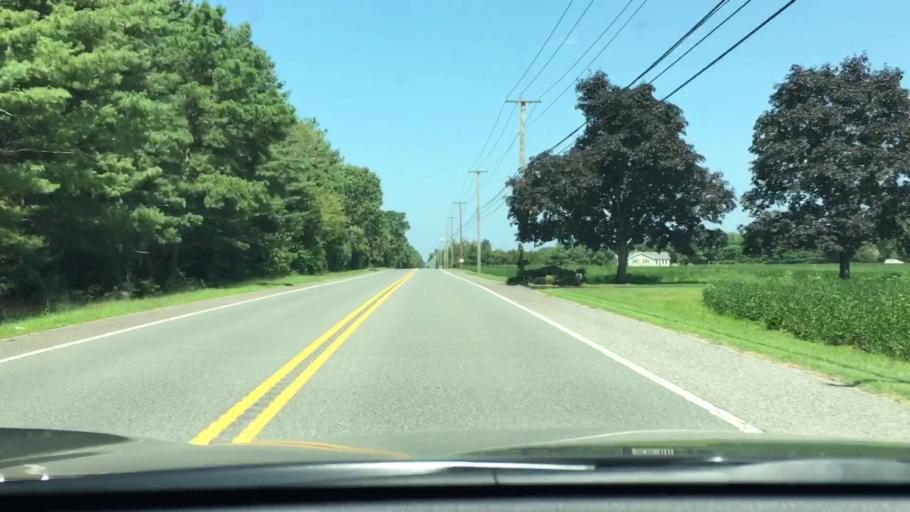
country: US
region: New Jersey
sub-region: Cumberland County
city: Laurel Lake
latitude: 39.2947
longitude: -74.9983
